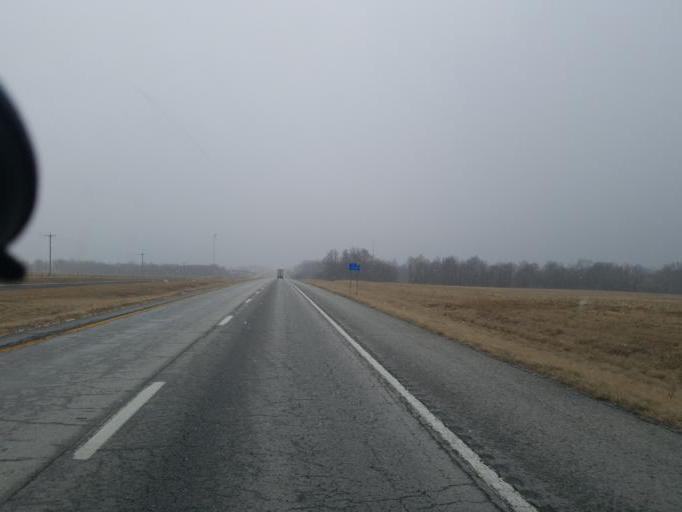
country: US
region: Missouri
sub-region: Macon County
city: La Plata
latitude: 39.9288
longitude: -92.4758
